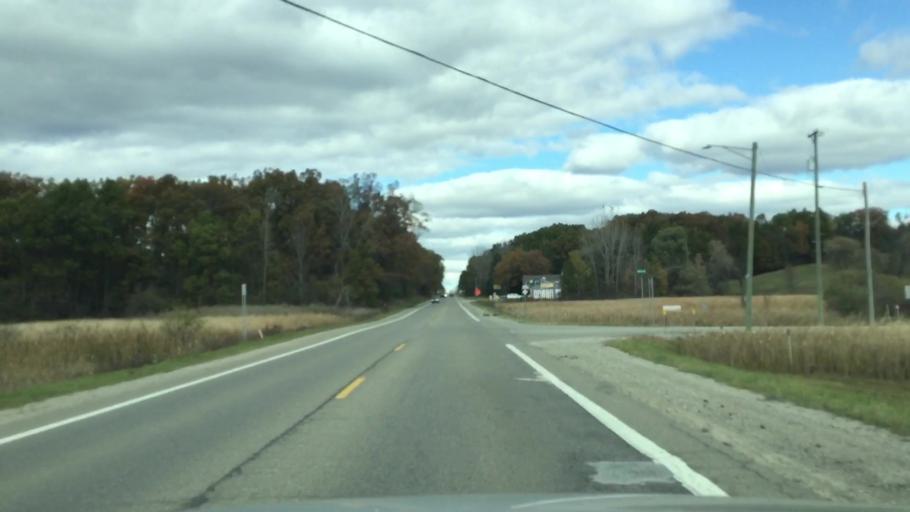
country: US
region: Michigan
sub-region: Lapeer County
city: Barnes Lake-Millers Lake
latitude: 43.1675
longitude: -83.3119
